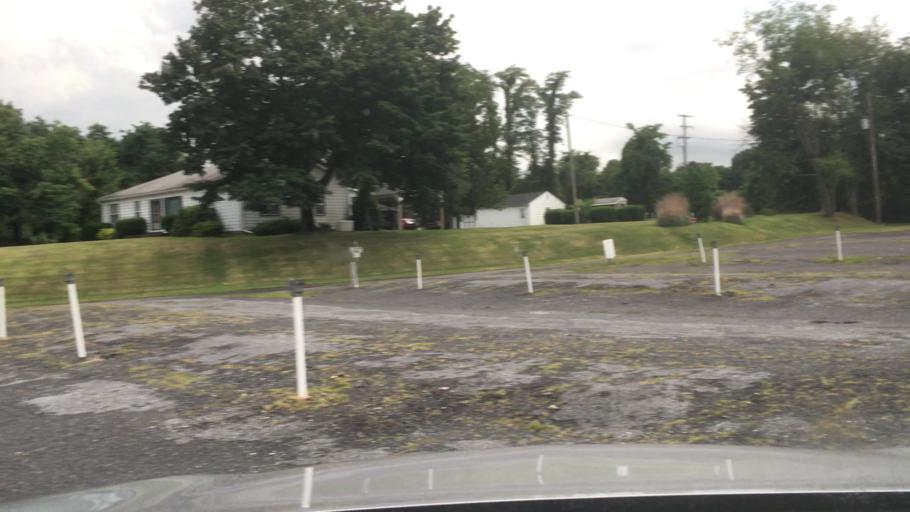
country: US
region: Pennsylvania
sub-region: York County
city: Dillsburg
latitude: 40.1253
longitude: -77.0203
